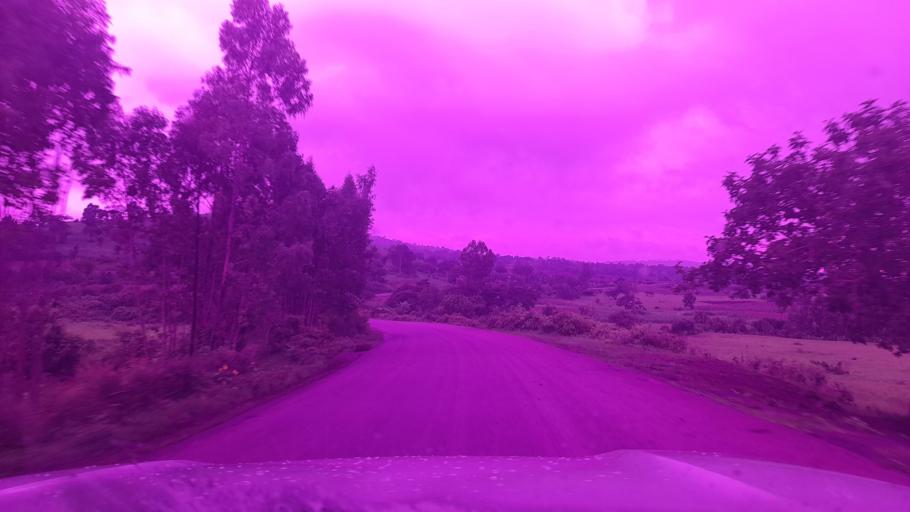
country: ET
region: Oromiya
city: Jima
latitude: 7.7853
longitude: 37.3410
